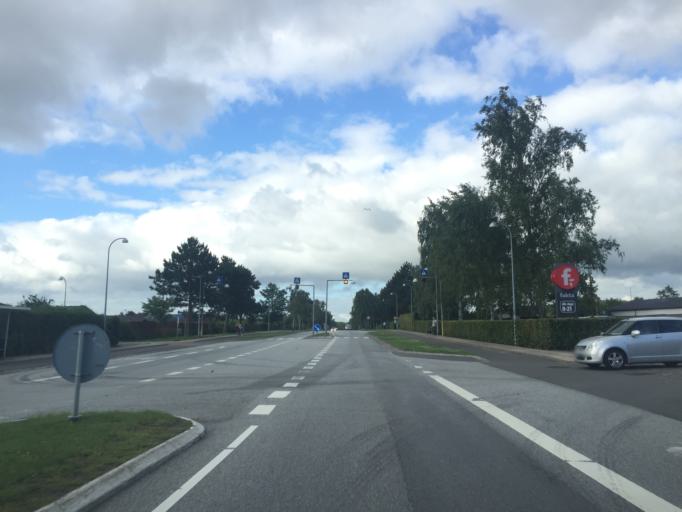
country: DK
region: Capital Region
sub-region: Brondby Kommune
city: Brondbyvester
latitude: 55.6587
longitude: 12.4316
